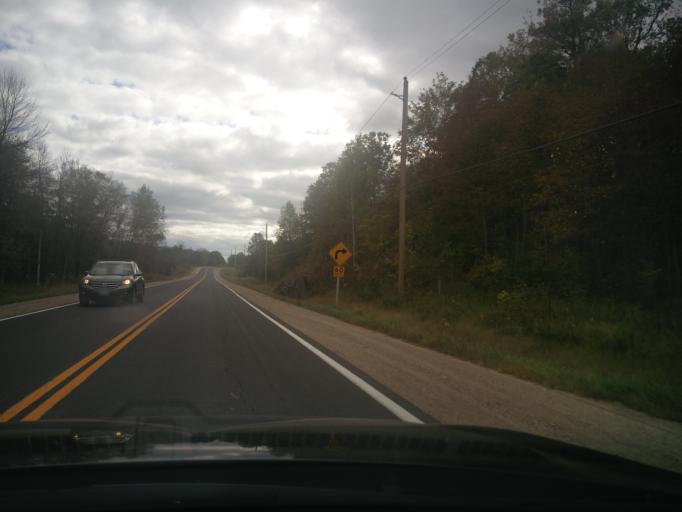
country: CA
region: Ontario
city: Perth
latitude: 44.8220
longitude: -76.3180
